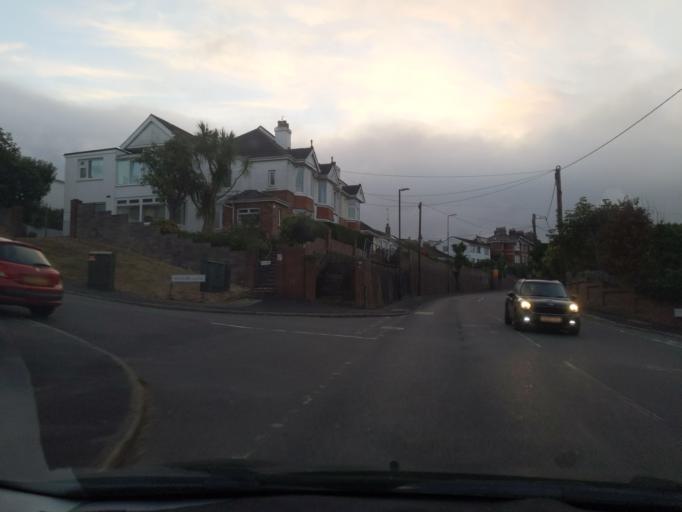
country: GB
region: England
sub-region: Borough of Torbay
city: Paignton
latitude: 50.4408
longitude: -3.5802
